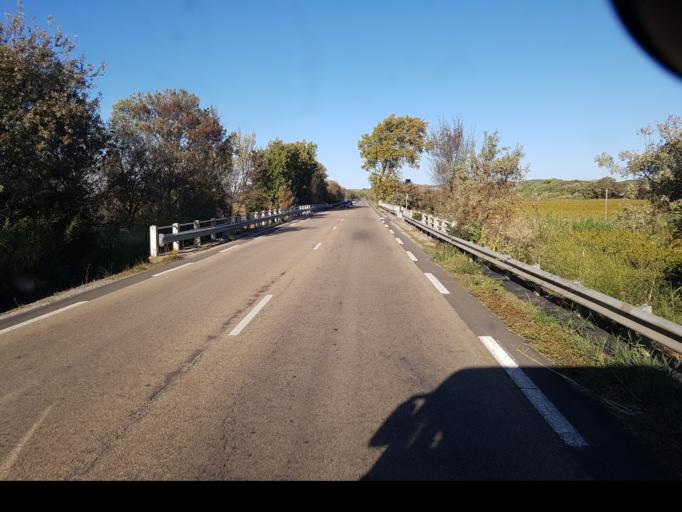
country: FR
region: Languedoc-Roussillon
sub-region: Departement de l'Aude
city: Coursan
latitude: 43.2522
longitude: 3.0703
